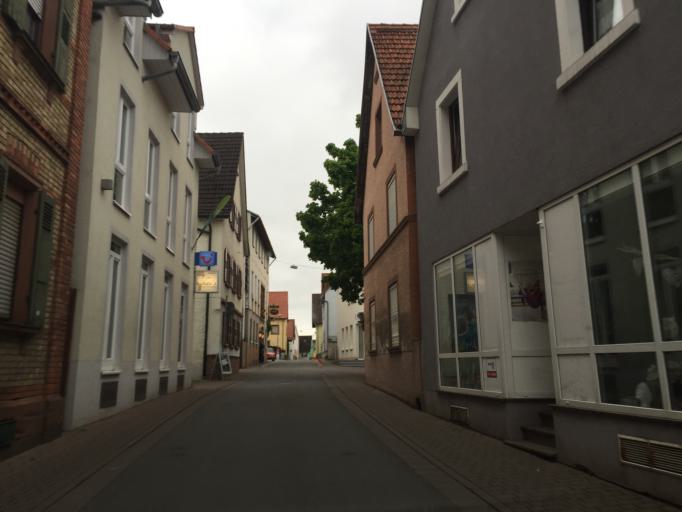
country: DE
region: Baden-Wuerttemberg
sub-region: Karlsruhe Region
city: Schriesheim
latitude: 49.5000
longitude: 8.6625
